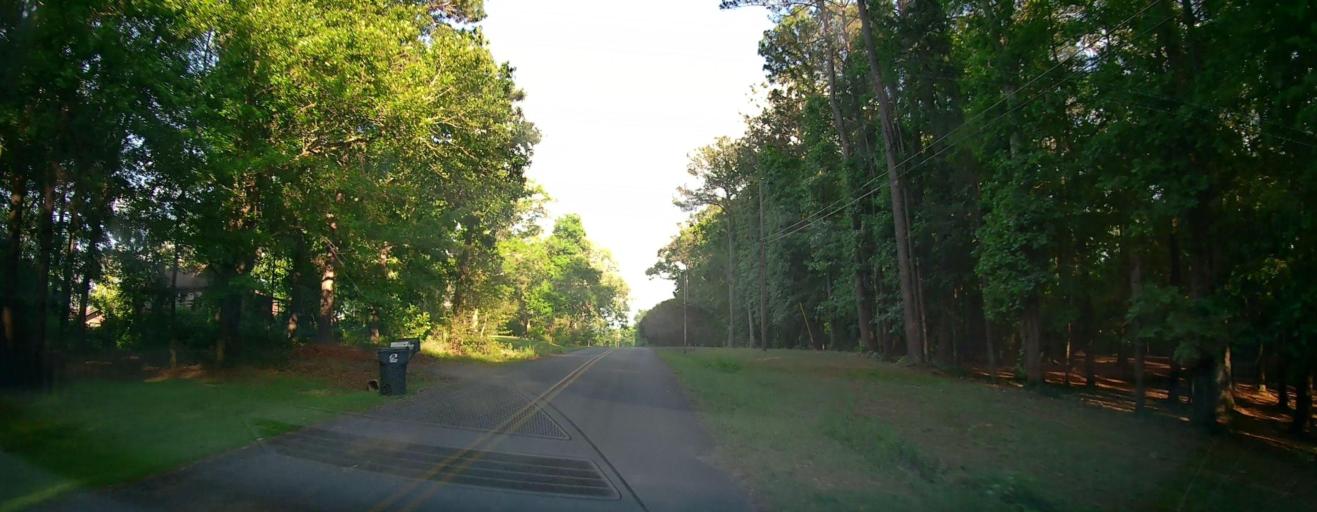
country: US
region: Georgia
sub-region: Peach County
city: Byron
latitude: 32.6436
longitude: -83.7525
